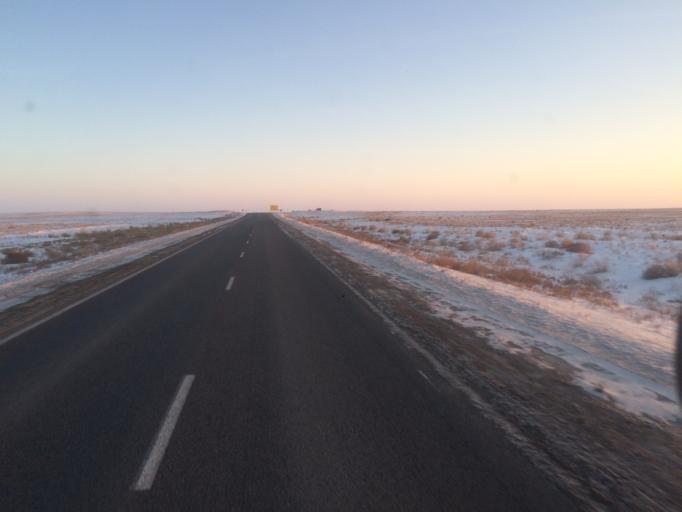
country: KZ
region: Qyzylorda
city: Sekseuil
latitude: 47.6432
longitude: 61.4762
